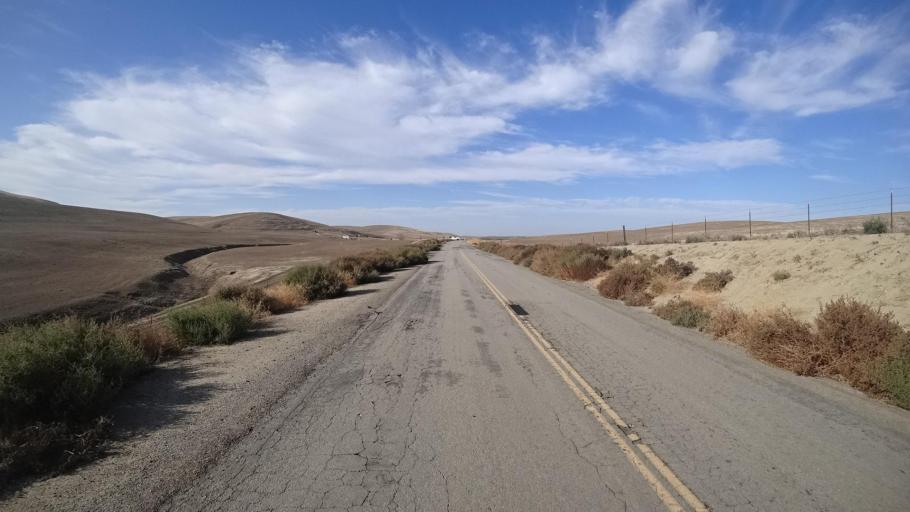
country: US
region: California
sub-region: Tulare County
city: Richgrove
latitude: 35.6211
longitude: -119.0178
